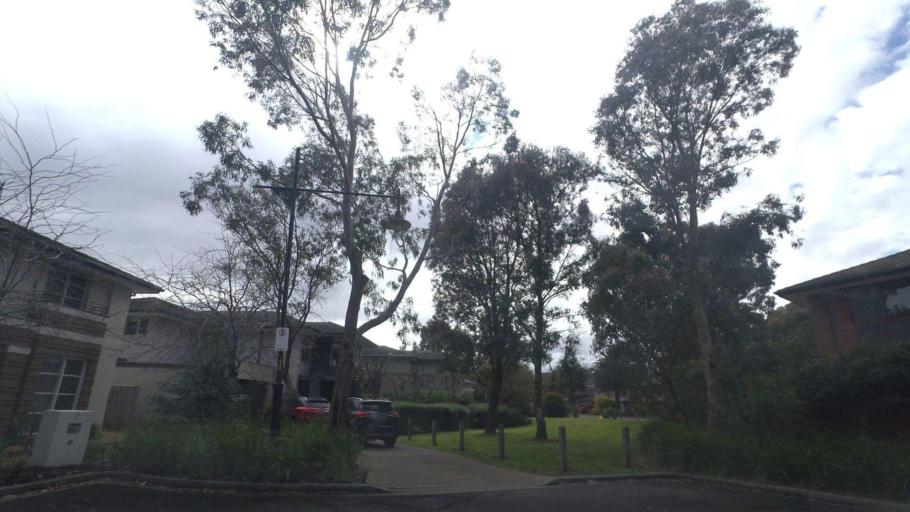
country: AU
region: Victoria
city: Macleod
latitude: -37.7180
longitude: 145.0598
